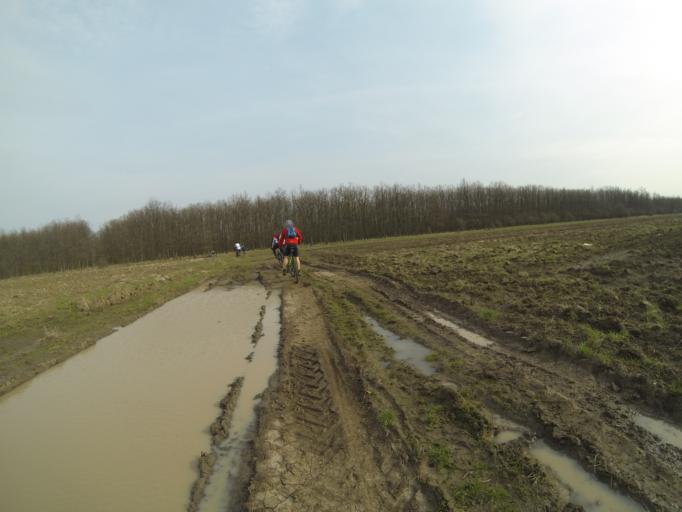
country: RO
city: Varvoru
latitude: 44.2581
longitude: 23.6859
